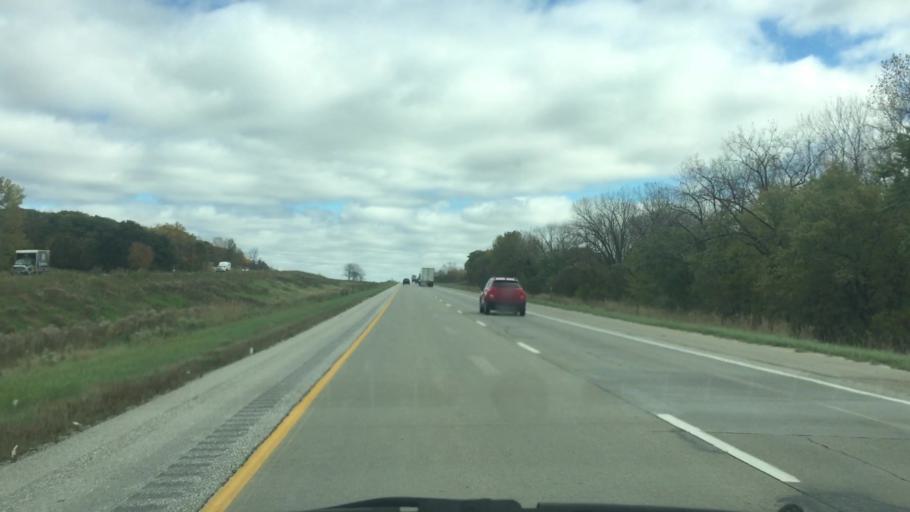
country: US
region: Iowa
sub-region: Jasper County
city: Colfax
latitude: 41.6852
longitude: -93.2847
